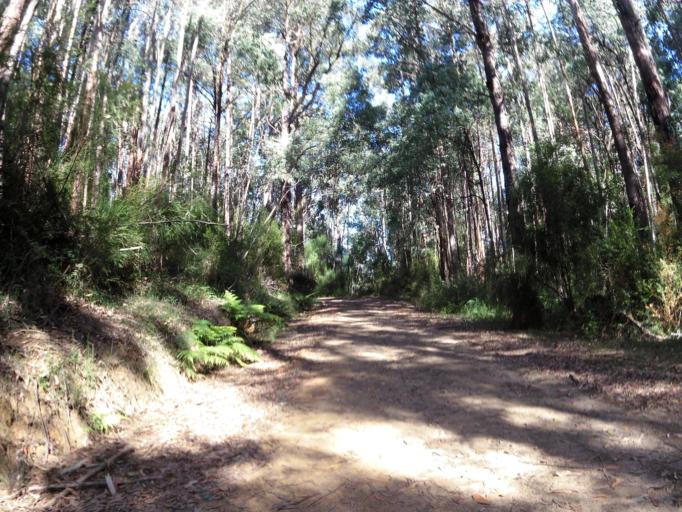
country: AU
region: Victoria
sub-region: Yarra Ranges
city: Millgrove
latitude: -37.8550
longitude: 145.7780
